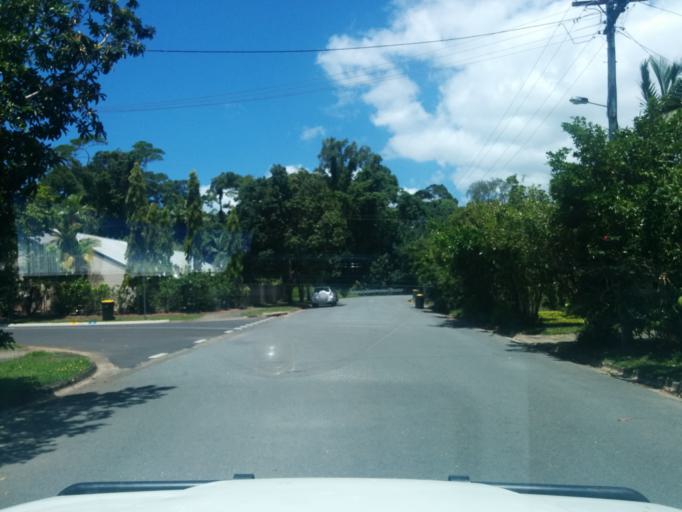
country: AU
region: Queensland
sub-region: Cairns
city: Cairns
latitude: -16.9016
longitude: 145.7456
